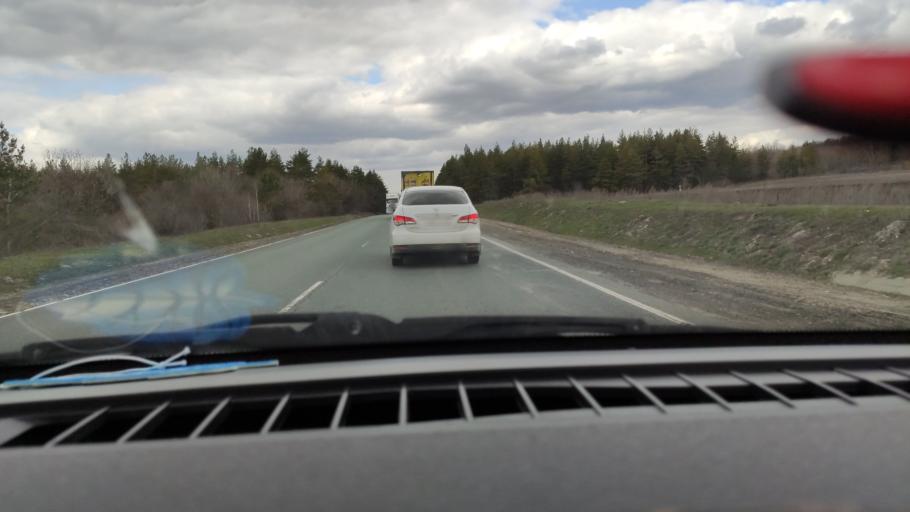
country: RU
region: Saratov
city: Vol'sk
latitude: 52.1049
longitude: 47.4393
